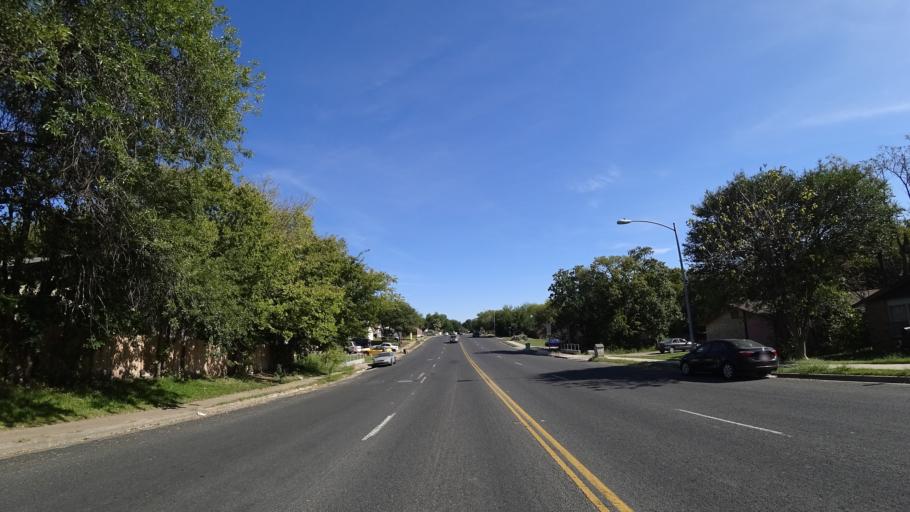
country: US
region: Texas
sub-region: Travis County
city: Austin
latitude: 30.2006
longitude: -97.7502
